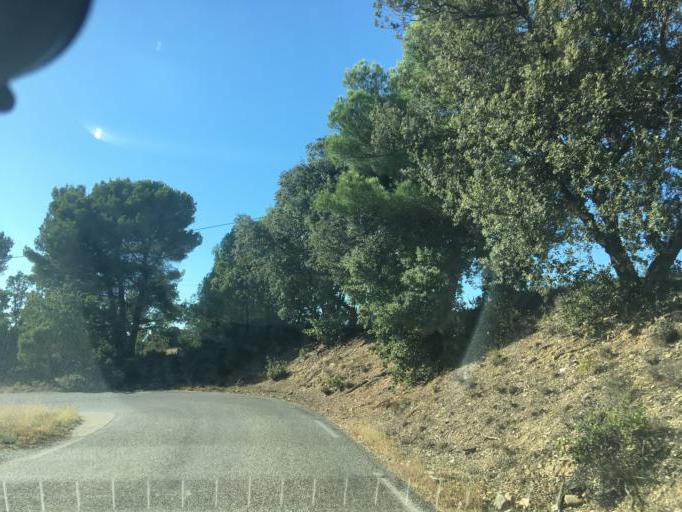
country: FR
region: Provence-Alpes-Cote d'Azur
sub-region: Departement du Var
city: Regusse
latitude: 43.7060
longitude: 6.1427
